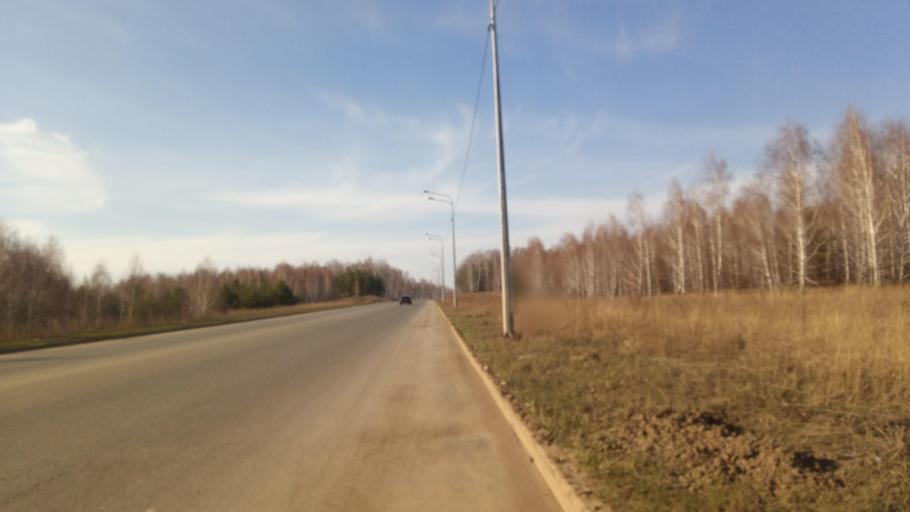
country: RU
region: Chelyabinsk
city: Sargazy
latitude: 55.1170
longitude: 61.2540
